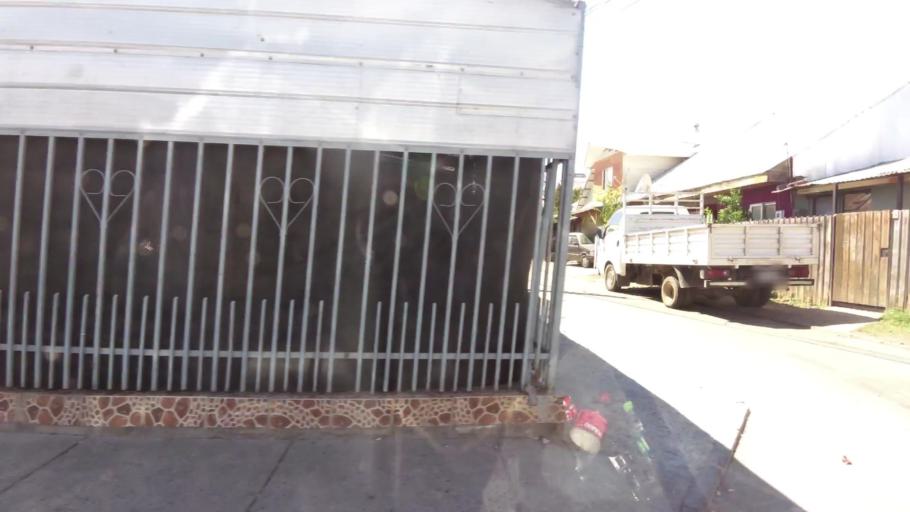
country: CL
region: Maule
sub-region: Provincia de Curico
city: Curico
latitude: -34.9659
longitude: -71.2367
